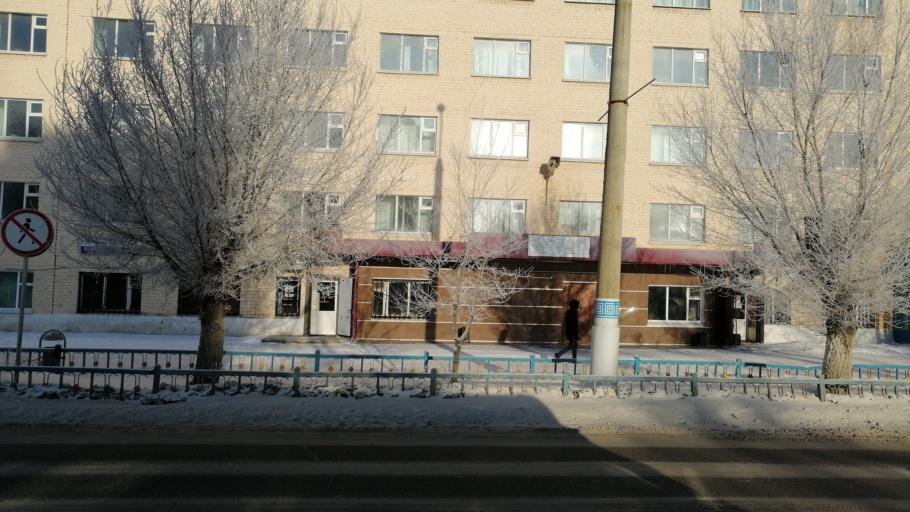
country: KZ
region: Aqtoebe
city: Aqtobe
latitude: 50.3010
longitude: 57.1522
